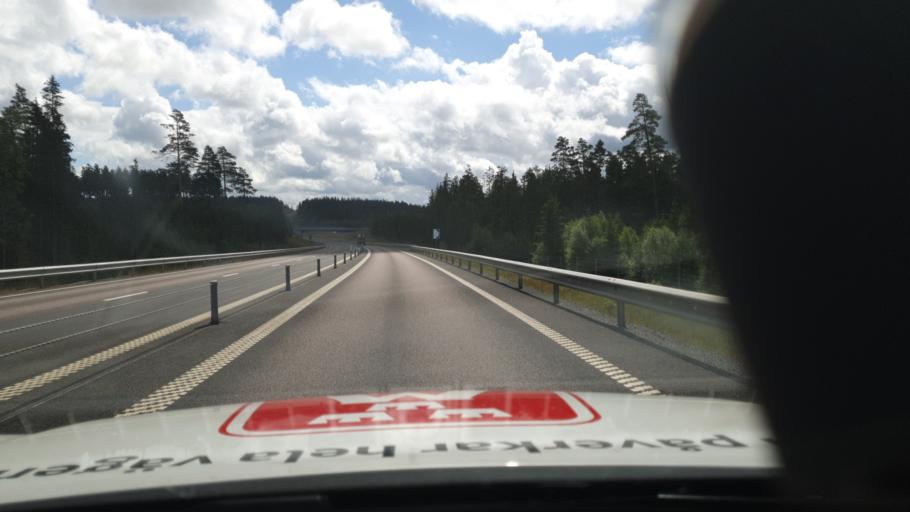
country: SE
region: Joenkoeping
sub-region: Mullsjo Kommun
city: Mullsjoe
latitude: 57.8899
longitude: 13.8903
